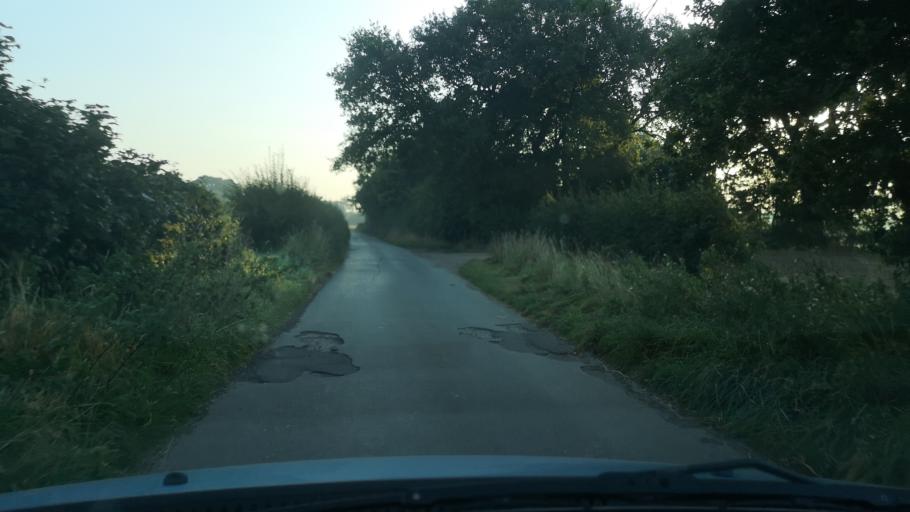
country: GB
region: England
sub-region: Doncaster
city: Hatfield
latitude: 53.5728
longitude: -0.9823
